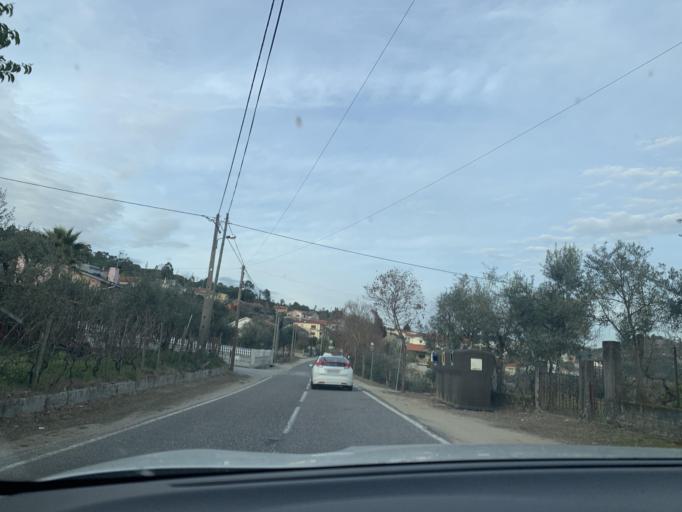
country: PT
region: Viseu
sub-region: Viseu
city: Viseu
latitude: 40.6038
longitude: -7.9834
